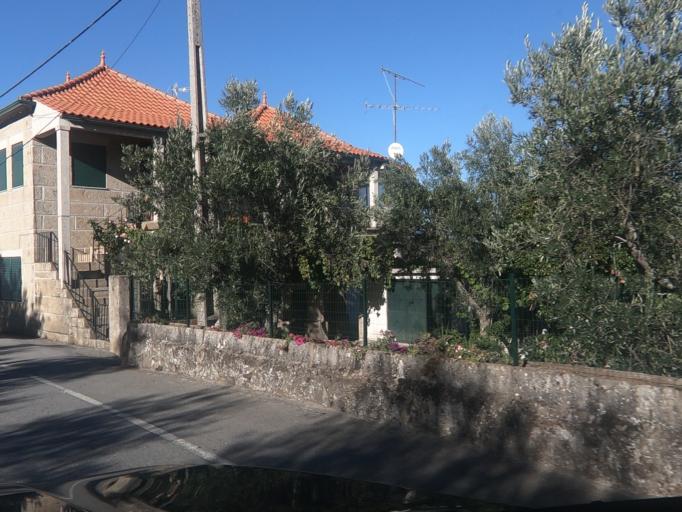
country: PT
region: Vila Real
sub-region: Sabrosa
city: Sabrosa
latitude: 41.3153
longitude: -7.5798
